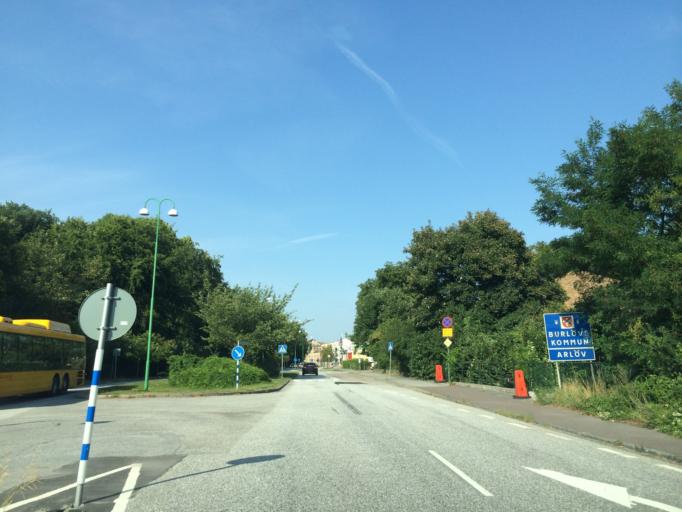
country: SE
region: Skane
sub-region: Burlovs Kommun
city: Arloev
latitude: 55.6284
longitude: 13.0670
